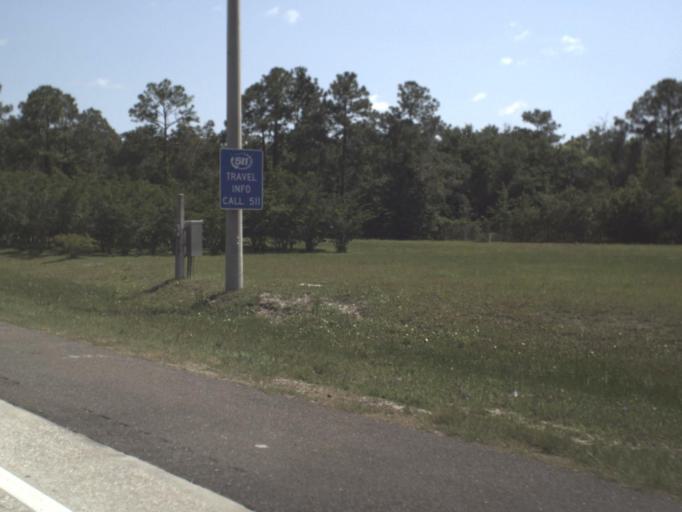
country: US
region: Florida
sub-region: Duval County
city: Jacksonville
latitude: 30.4102
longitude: -81.6572
